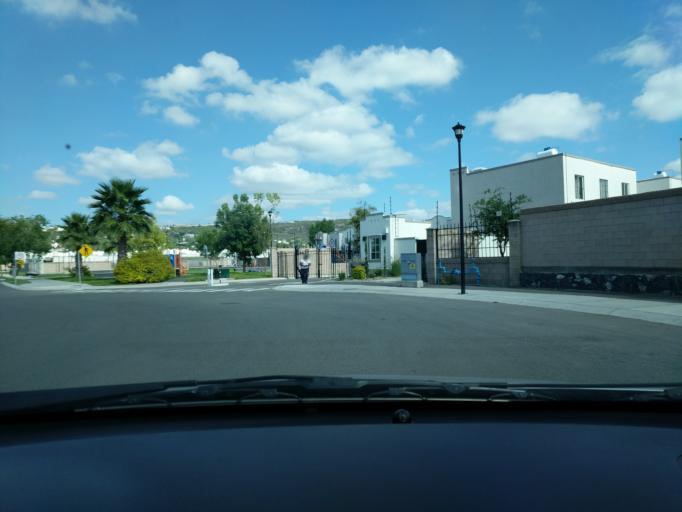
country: MX
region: Queretaro
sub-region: Queretaro
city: Patria Nueva
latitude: 20.6307
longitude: -100.4927
